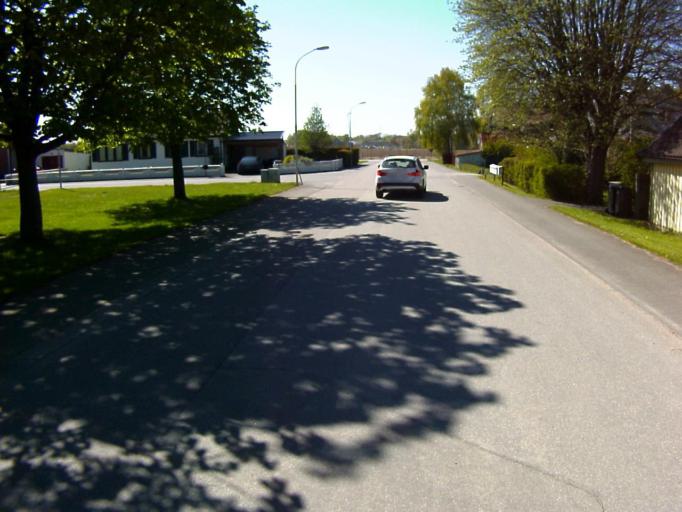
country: SE
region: Skane
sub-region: Kristianstads Kommun
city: Kristianstad
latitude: 56.0279
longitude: 14.1921
